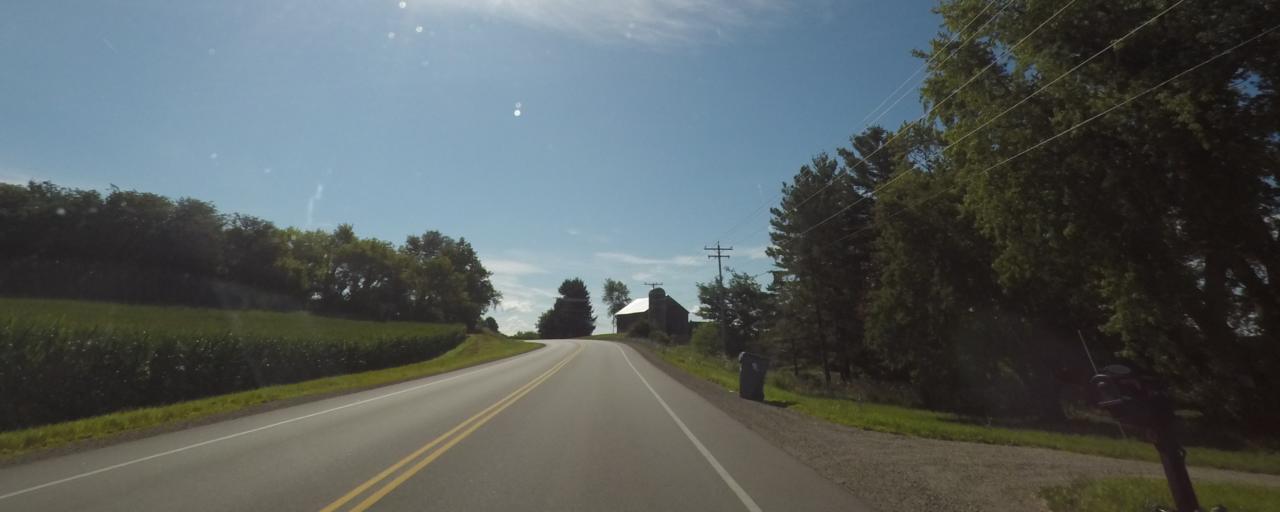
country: US
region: Wisconsin
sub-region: Jefferson County
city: Johnson Creek
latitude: 43.0766
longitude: -88.7461
